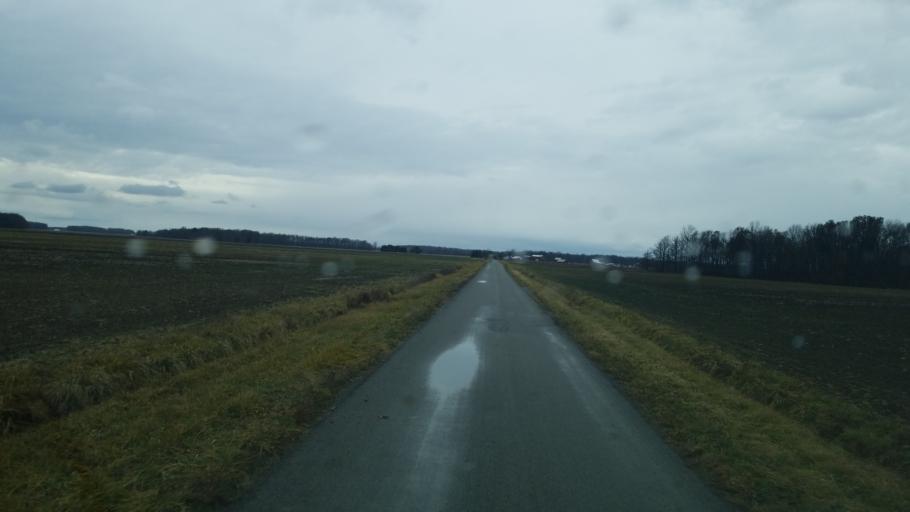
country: US
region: Ohio
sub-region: Hardin County
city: Forest
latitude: 40.7496
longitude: -83.4098
